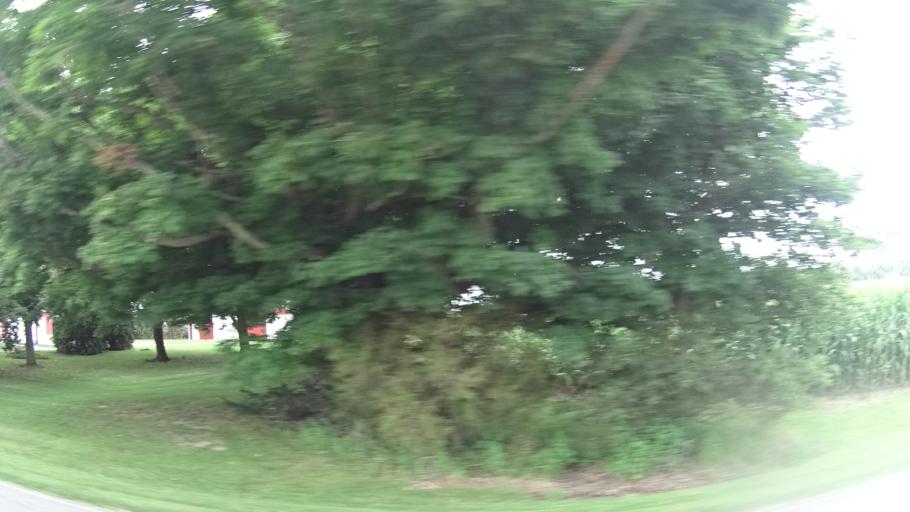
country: US
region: Indiana
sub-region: Madison County
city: Lapel
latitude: 40.0589
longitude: -85.8357
